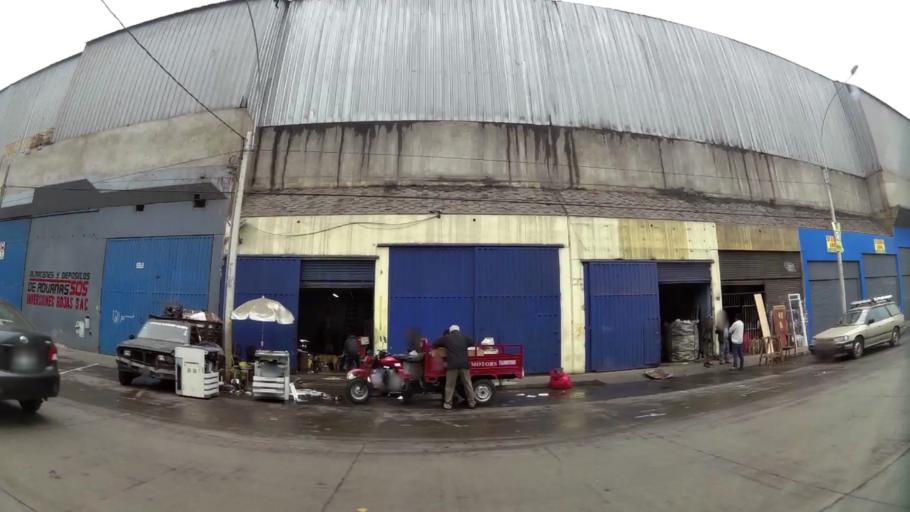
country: PE
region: Lima
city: Lima
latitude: -12.0646
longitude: -77.0226
